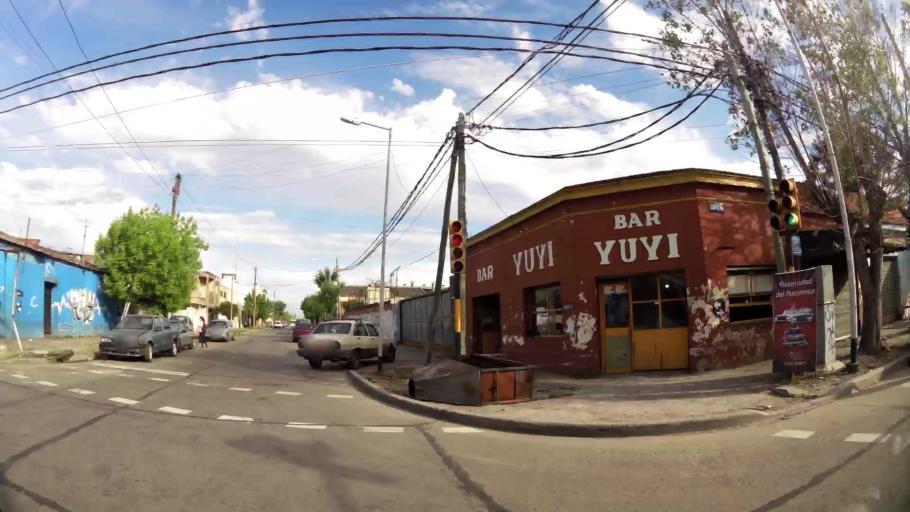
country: AR
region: Buenos Aires
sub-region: Partido de Lanus
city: Lanus
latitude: -34.7022
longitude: -58.3557
